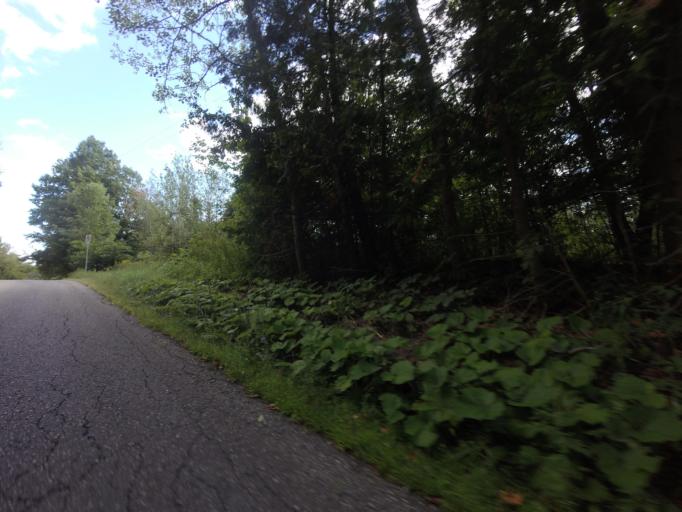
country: CA
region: Ontario
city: Orangeville
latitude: 43.8178
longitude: -79.9869
